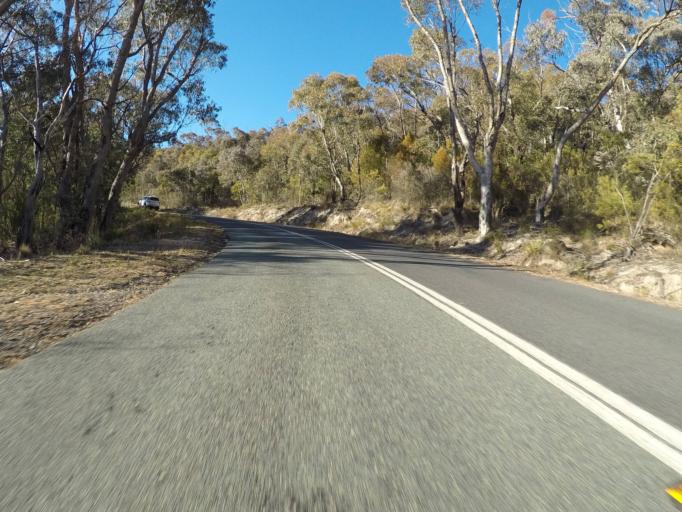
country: AU
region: Australian Capital Territory
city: Macarthur
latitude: -35.4822
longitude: 148.9321
